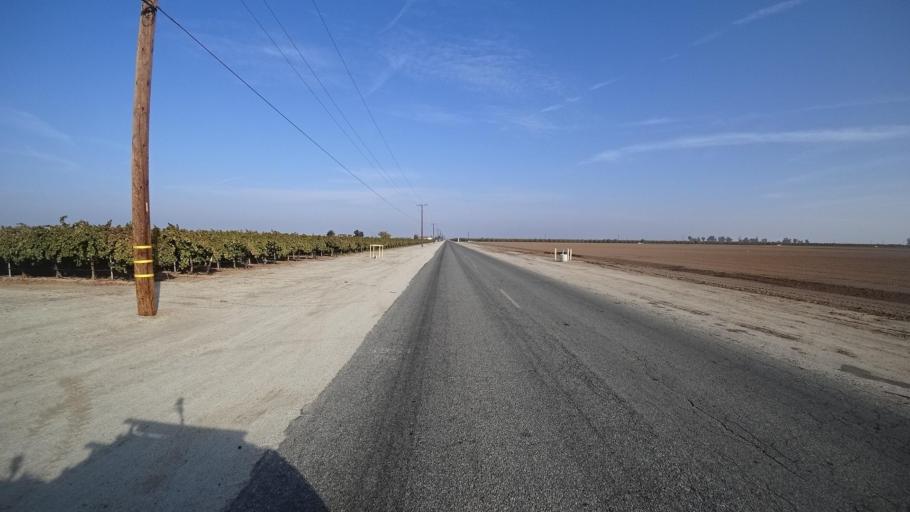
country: US
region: California
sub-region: Kern County
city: McFarland
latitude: 35.6788
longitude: -119.2046
